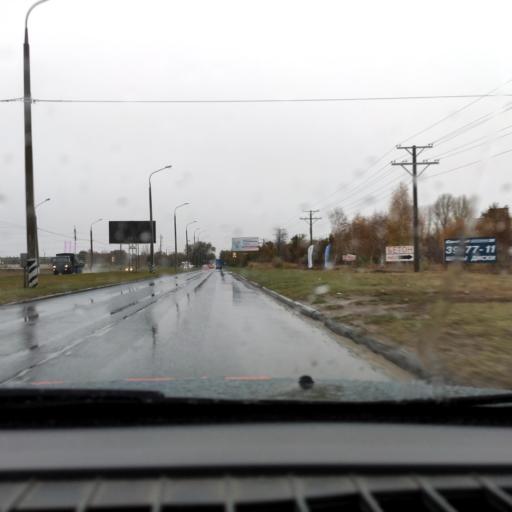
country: RU
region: Samara
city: Tol'yatti
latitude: 53.5582
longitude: 49.3247
